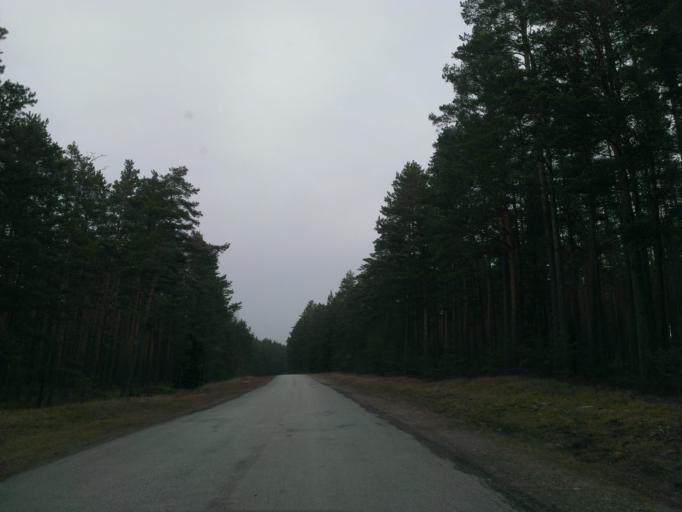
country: LV
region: Salacgrivas
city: Ainazi
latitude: 57.9794
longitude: 24.4153
